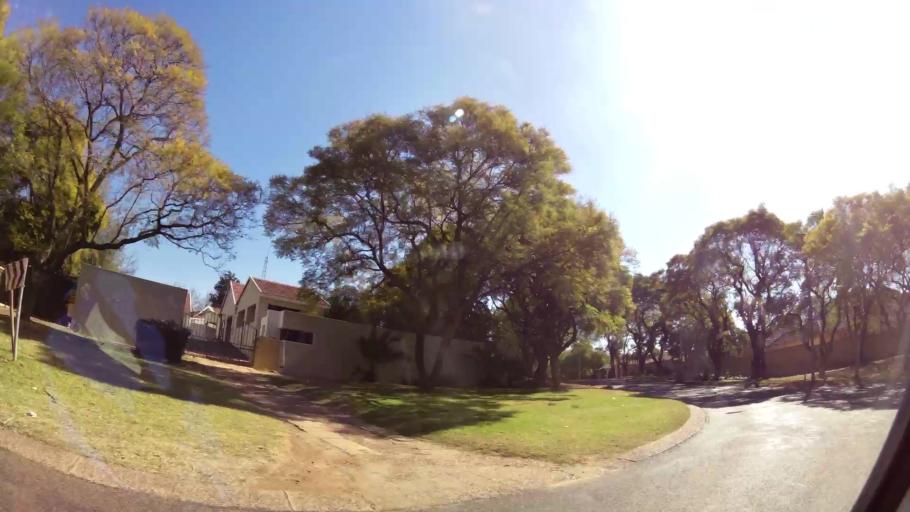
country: ZA
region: Gauteng
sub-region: City of Tshwane Metropolitan Municipality
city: Pretoria
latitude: -25.7901
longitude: 28.2408
